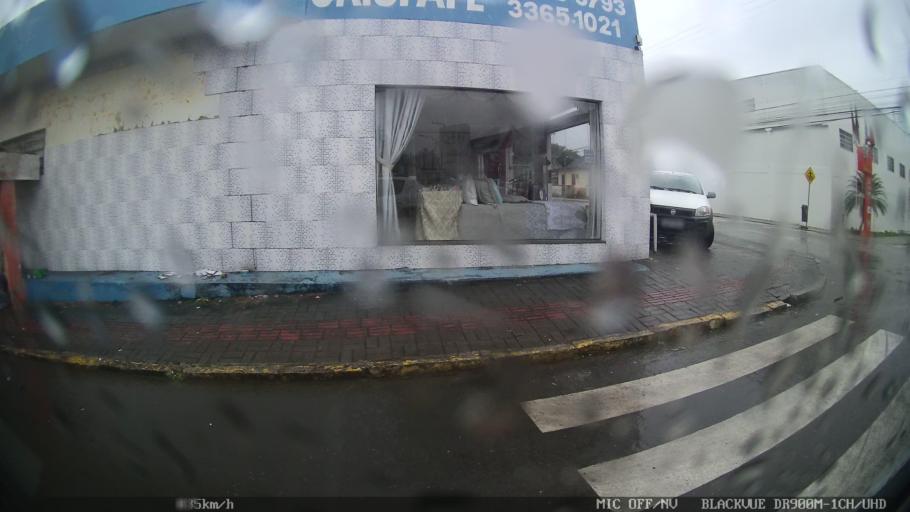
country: BR
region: Santa Catarina
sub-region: Balneario Camboriu
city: Balneario Camboriu
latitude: -27.0239
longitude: -48.6487
